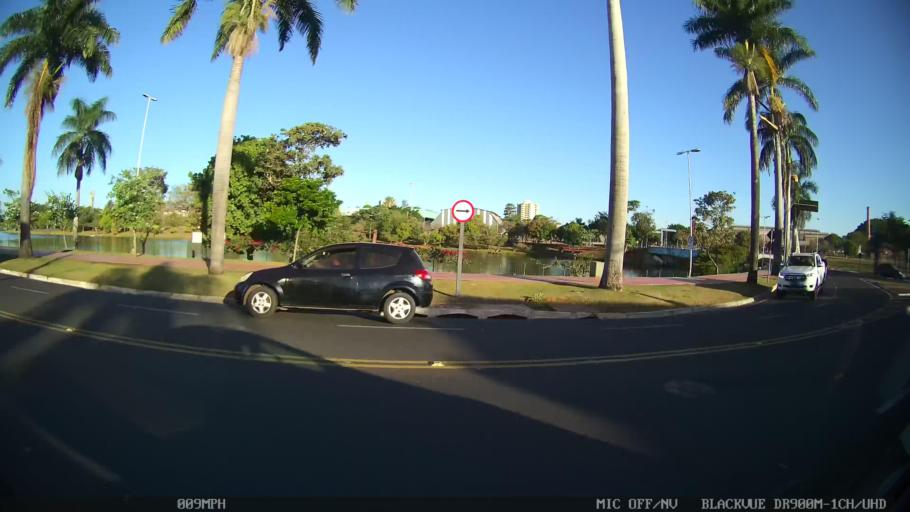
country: BR
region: Sao Paulo
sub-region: Sao Jose Do Rio Preto
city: Sao Jose do Rio Preto
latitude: -20.8083
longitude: -49.3678
